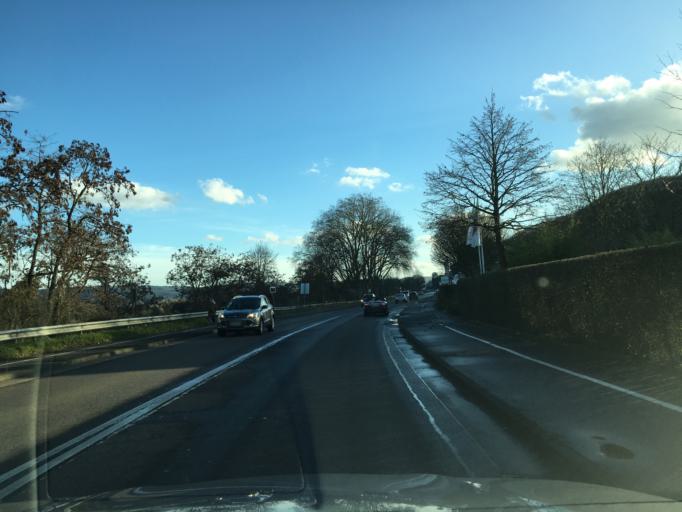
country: DE
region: North Rhine-Westphalia
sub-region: Regierungsbezirk Koln
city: Bad Honnef
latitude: 50.6516
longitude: 7.1988
